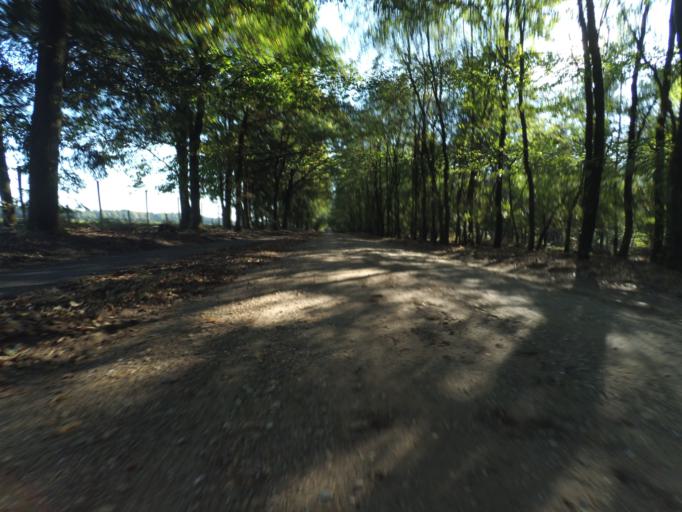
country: NL
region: Gelderland
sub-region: Gemeente Apeldoorn
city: Uddel
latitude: 52.2054
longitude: 5.8252
